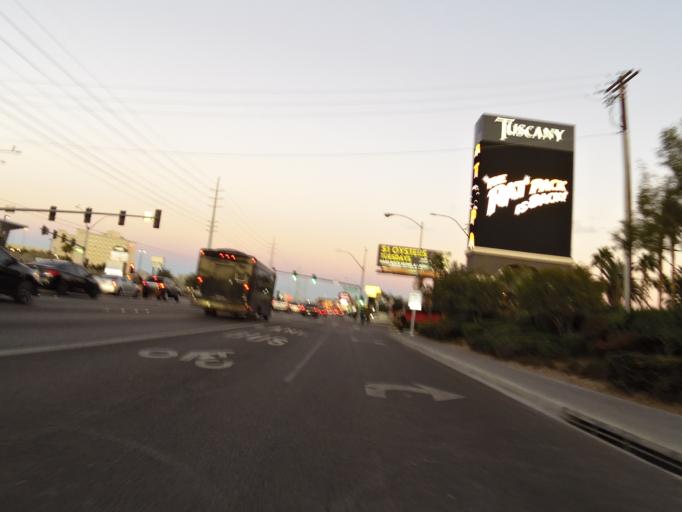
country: US
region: Nevada
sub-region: Clark County
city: Paradise
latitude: 36.1143
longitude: -115.1598
